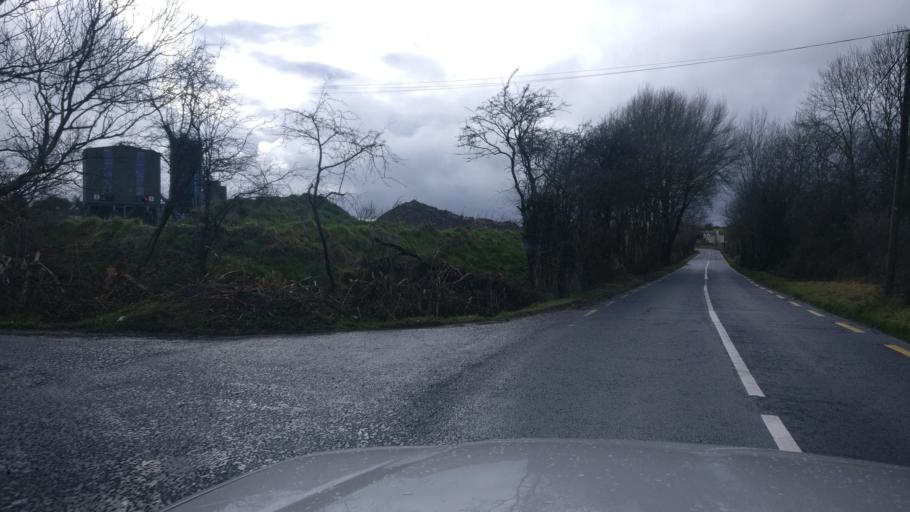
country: IE
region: Leinster
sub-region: An Iarmhi
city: Athlone
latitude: 53.4239
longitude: -8.0353
